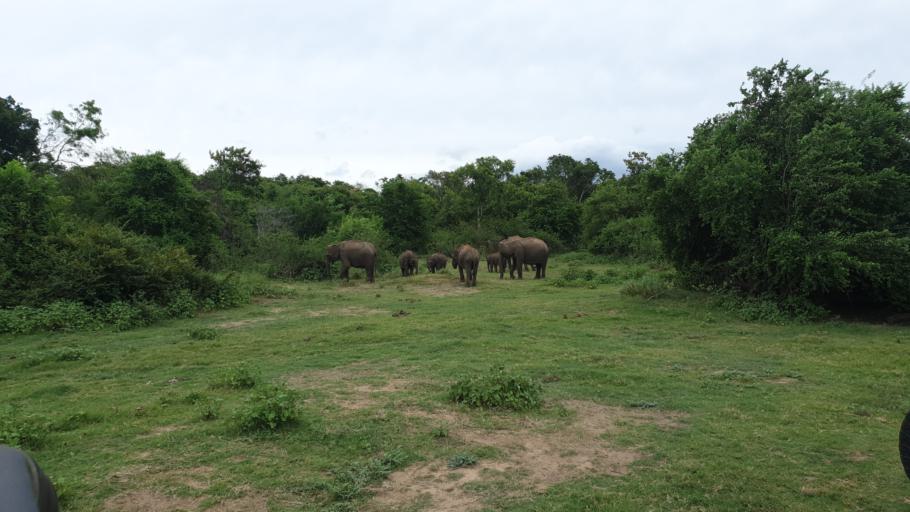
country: LK
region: North Central
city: Polonnaruwa
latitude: 8.1298
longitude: 80.9024
